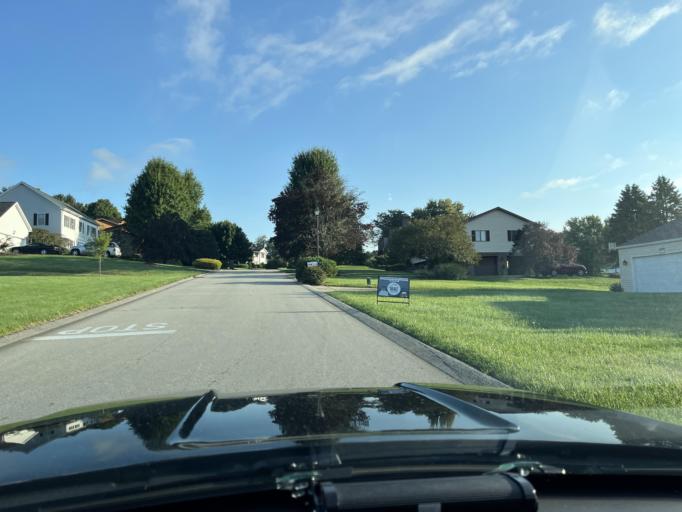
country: US
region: Pennsylvania
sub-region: Fayette County
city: Leith-Hatfield
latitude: 39.8744
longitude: -79.7272
